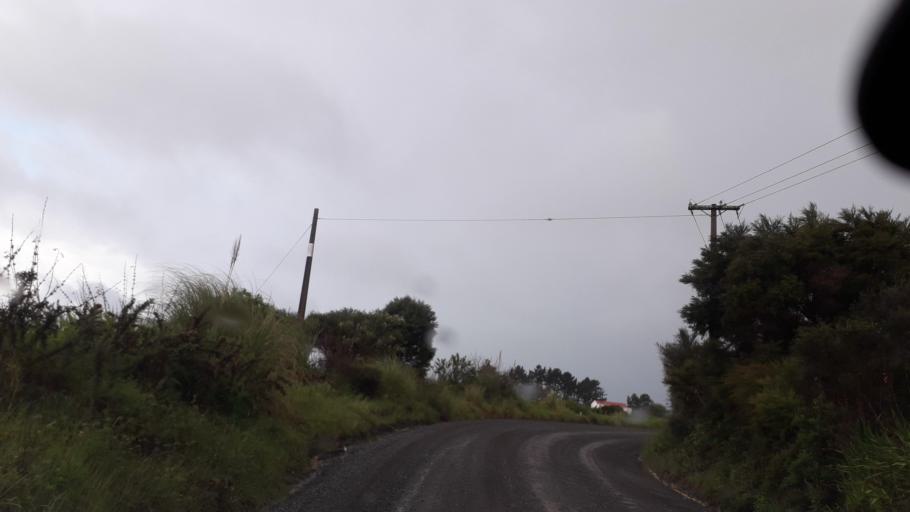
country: NZ
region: Northland
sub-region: Far North District
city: Kerikeri
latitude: -35.1353
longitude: 173.9983
